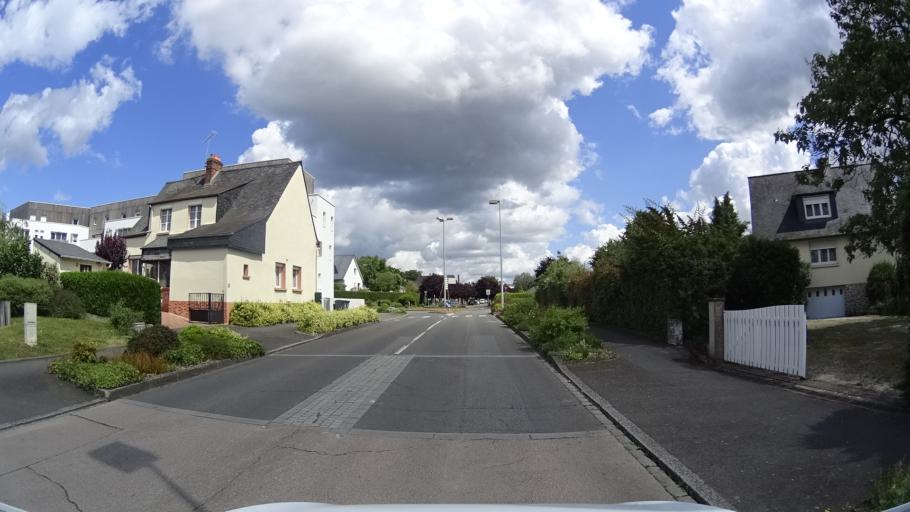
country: FR
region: Brittany
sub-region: Departement d'Ille-et-Vilaine
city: Chartres-de-Bretagne
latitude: 48.0371
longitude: -1.7065
